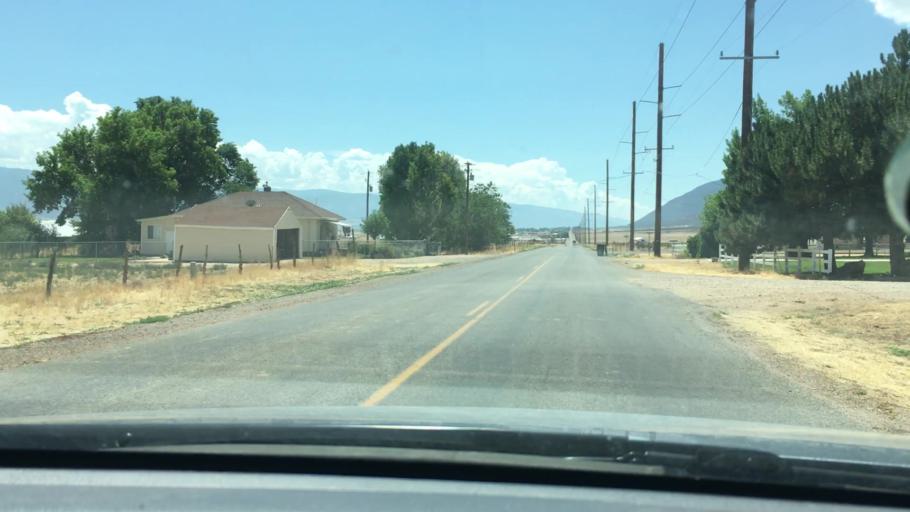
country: US
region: Utah
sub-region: Sanpete County
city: Moroni
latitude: 39.5430
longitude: -111.6400
